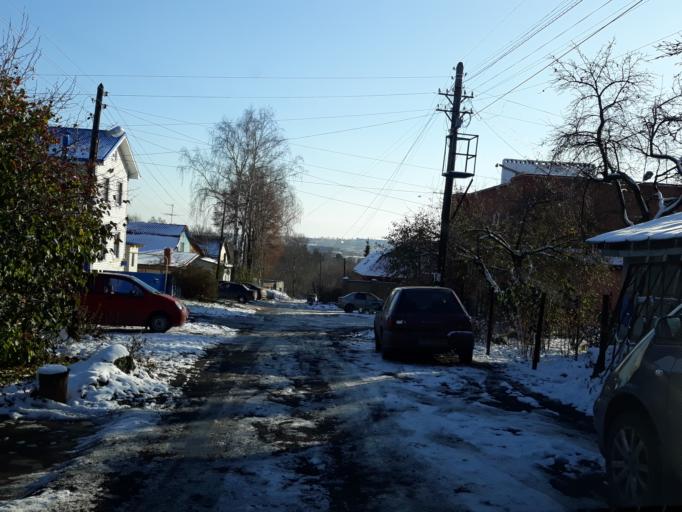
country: RU
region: Nizjnij Novgorod
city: Nizhniy Novgorod
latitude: 56.2536
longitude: 43.9993
